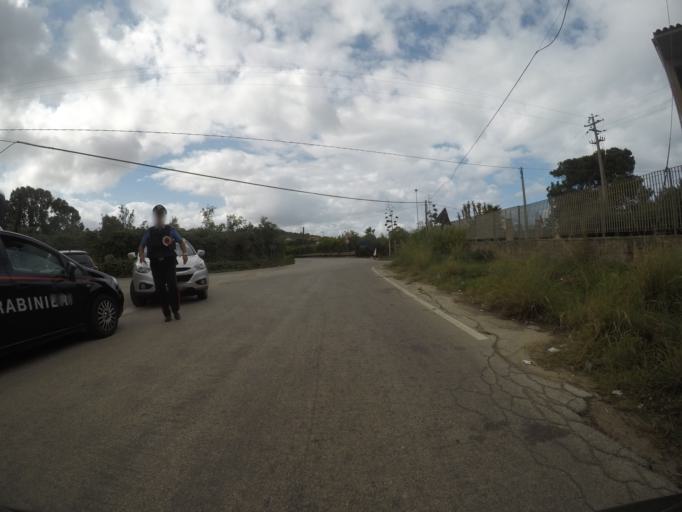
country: IT
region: Sicily
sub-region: Palermo
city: Trappeto
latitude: 38.0711
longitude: 13.0559
